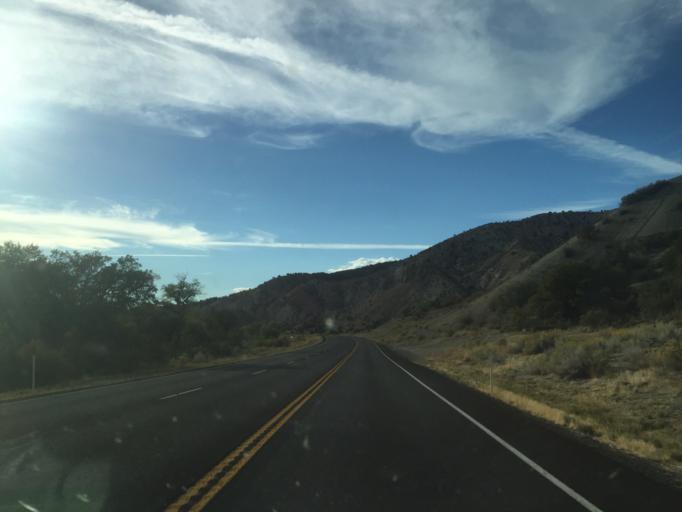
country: US
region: Utah
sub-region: Juab County
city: Nephi
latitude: 39.7127
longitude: -111.7805
